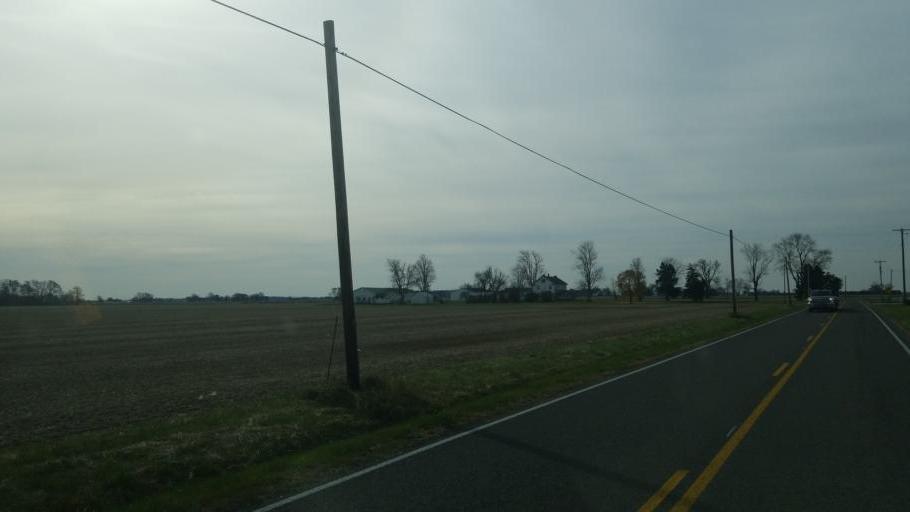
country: US
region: Ohio
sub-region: Madison County
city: Plain City
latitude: 40.1035
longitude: -83.2914
